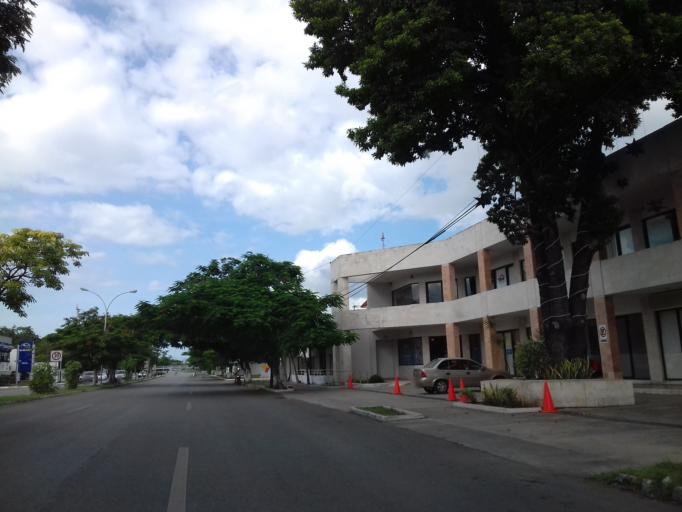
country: MX
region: Yucatan
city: Merida
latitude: 20.9960
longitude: -89.6162
